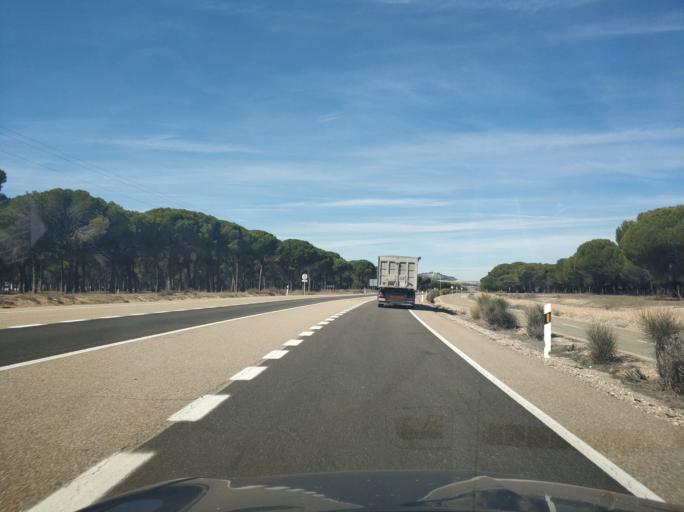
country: ES
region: Castille and Leon
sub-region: Provincia de Valladolid
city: Simancas
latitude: 41.5669
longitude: -4.8014
